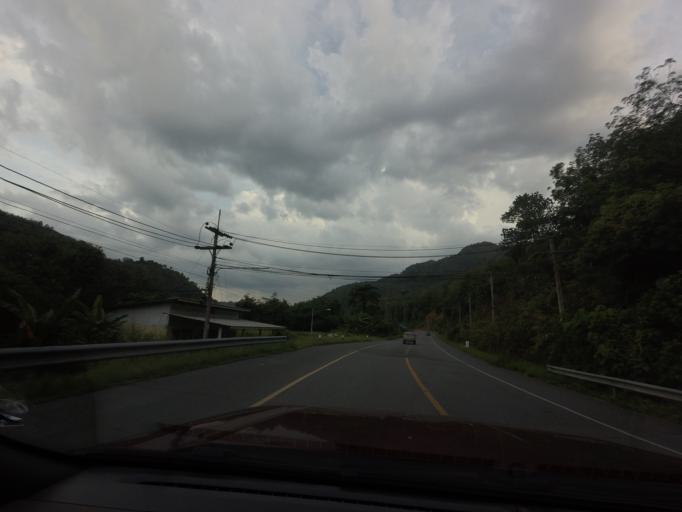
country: TH
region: Yala
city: Than To
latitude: 6.0015
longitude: 101.1931
